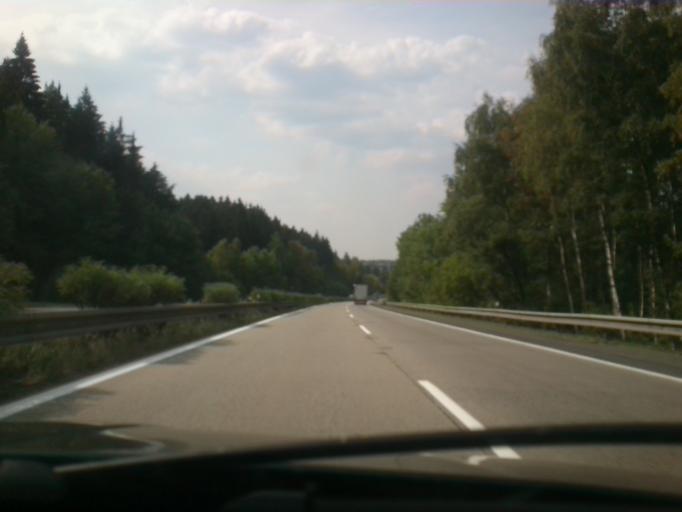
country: CZ
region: Central Bohemia
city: Divisov
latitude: 49.8111
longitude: 14.8844
